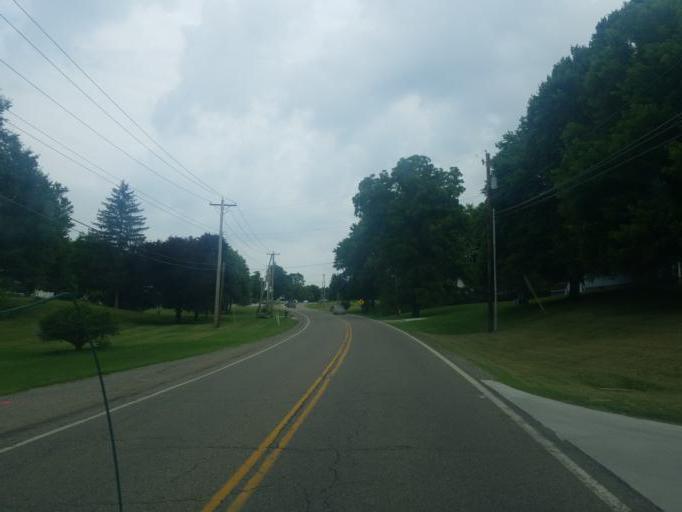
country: US
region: Ohio
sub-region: Carroll County
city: Carrollton
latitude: 40.5936
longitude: -81.0782
